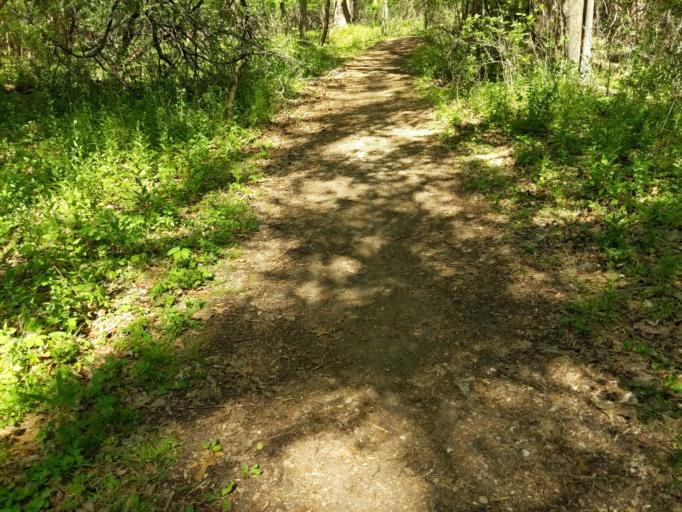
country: US
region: Michigan
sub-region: Kent County
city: Kentwood
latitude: 42.9095
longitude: -85.6497
